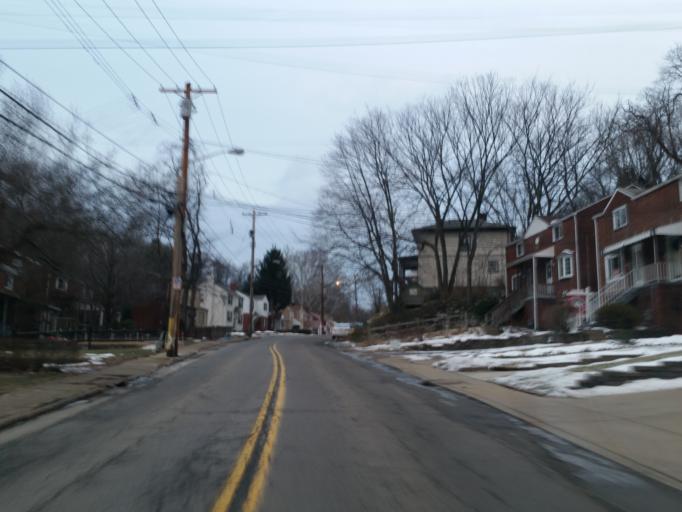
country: US
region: Pennsylvania
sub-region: Allegheny County
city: Brentwood
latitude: 40.3841
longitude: -79.9891
